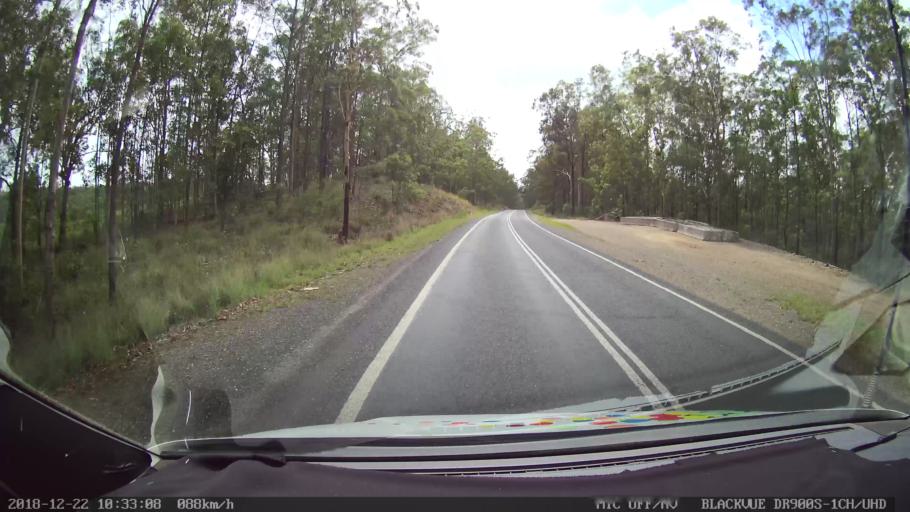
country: AU
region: New South Wales
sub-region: Clarence Valley
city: South Grafton
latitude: -29.6164
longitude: 152.6500
